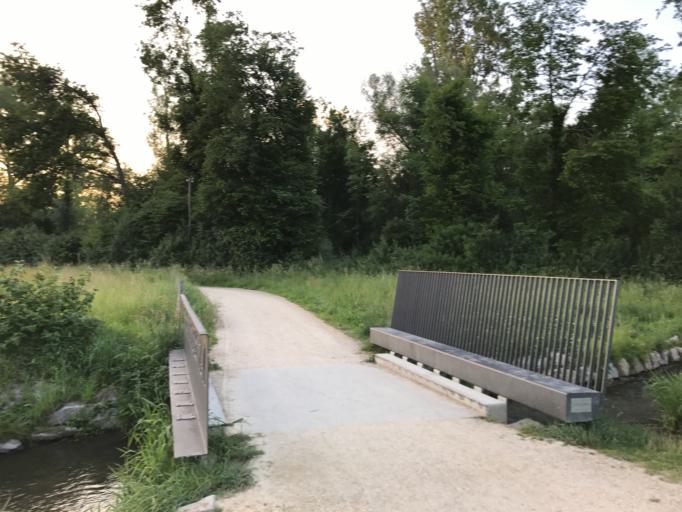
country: CH
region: Basel-City
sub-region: Basel-Stadt
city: Riehen
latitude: 47.5797
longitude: 7.6366
